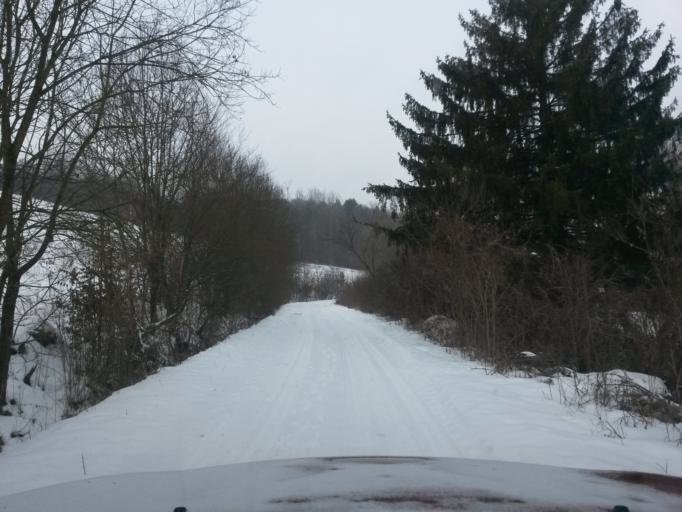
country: SK
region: Presovsky
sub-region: Okres Presov
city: Presov
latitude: 48.9144
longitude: 21.1806
